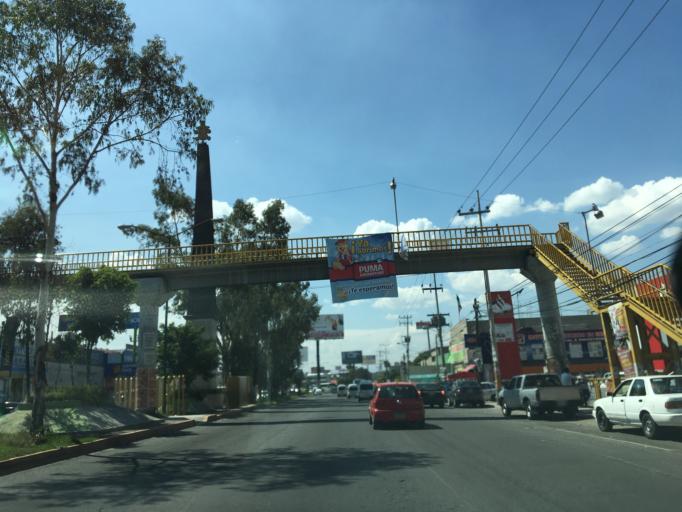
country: MX
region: Mexico
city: Los Reyes La Paz
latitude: 19.3563
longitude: -98.9833
